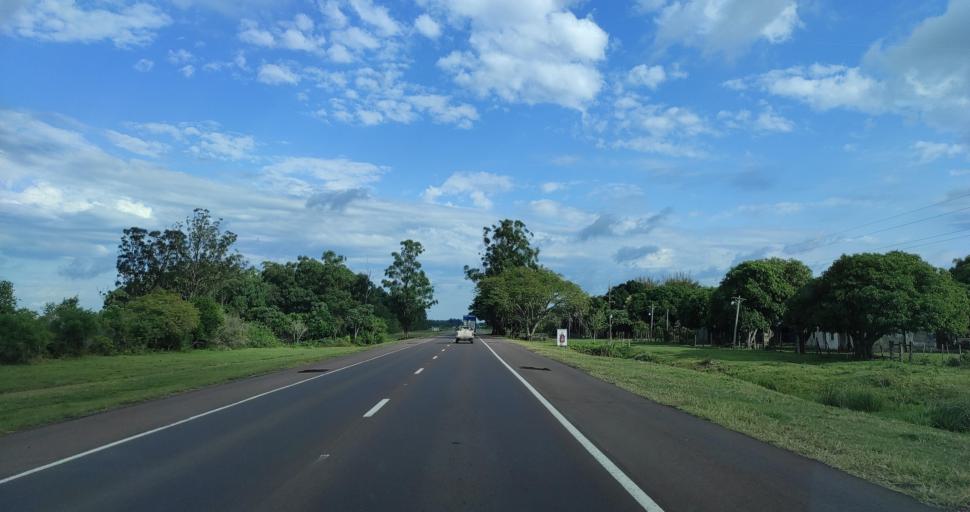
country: AR
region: Corrientes
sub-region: Departamento de Itati
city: Itati
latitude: -27.3672
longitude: -58.3599
